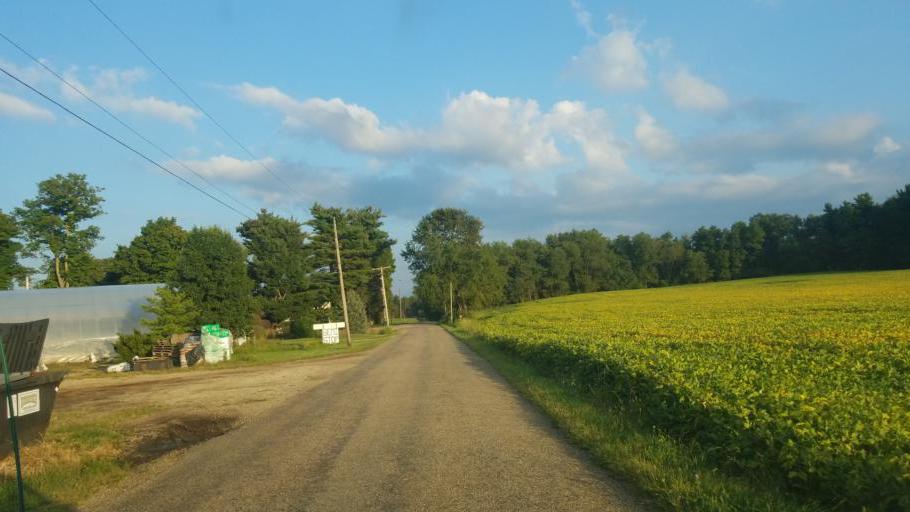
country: US
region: Ohio
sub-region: Ashland County
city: Loudonville
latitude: 40.6536
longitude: -82.1997
